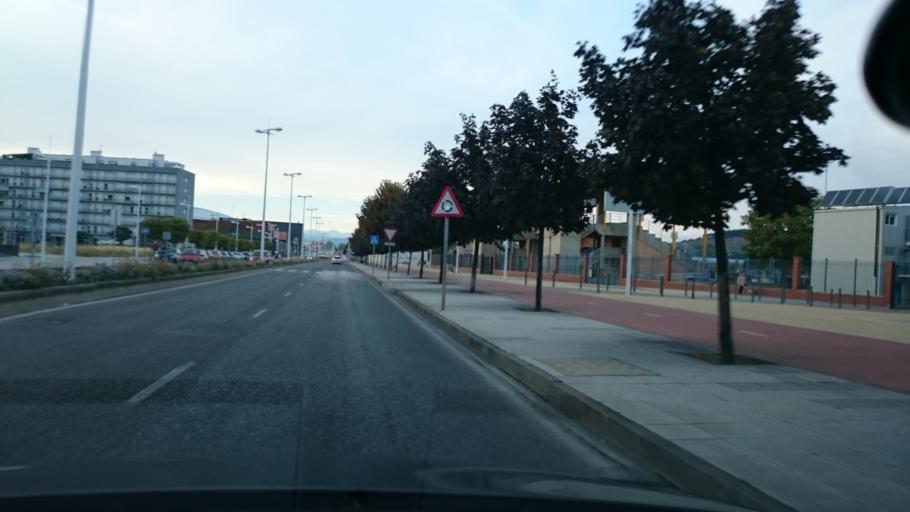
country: ES
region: Castille and Leon
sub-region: Provincia de Leon
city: Ponferrada
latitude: 42.5540
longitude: -6.6006
